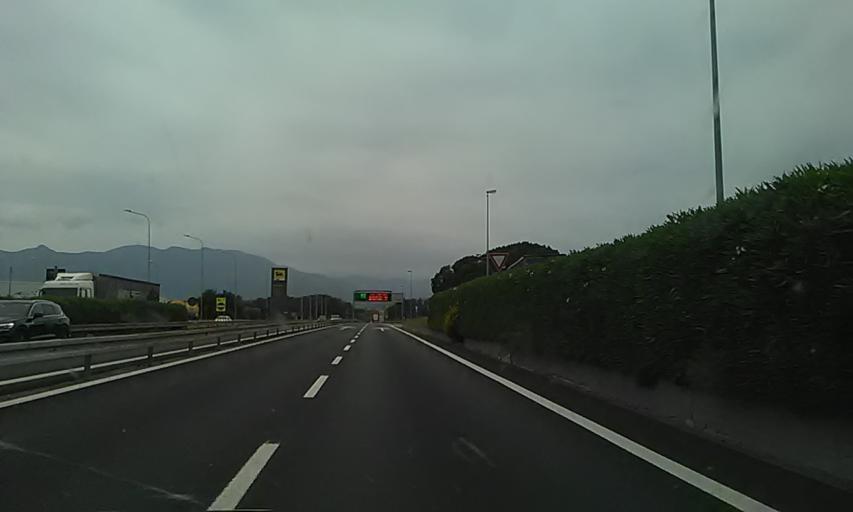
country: IT
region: Liguria
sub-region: Provincia di Savona
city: Campochiesa
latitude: 44.0883
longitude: 8.2062
